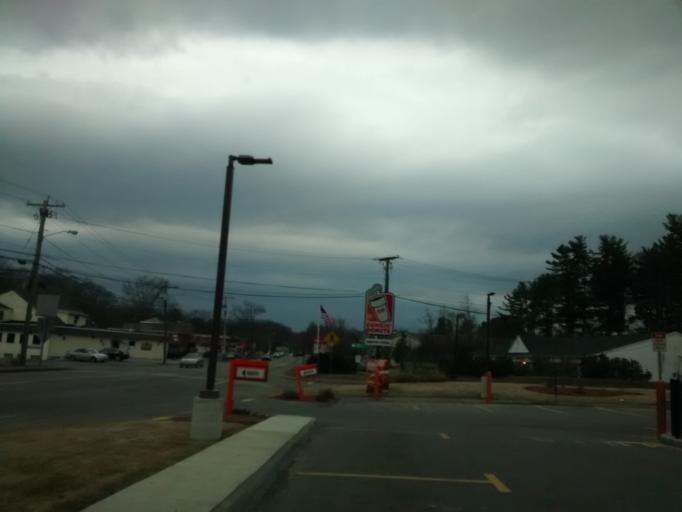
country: US
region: Massachusetts
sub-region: Worcester County
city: Grafton
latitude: 42.2152
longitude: -71.6920
